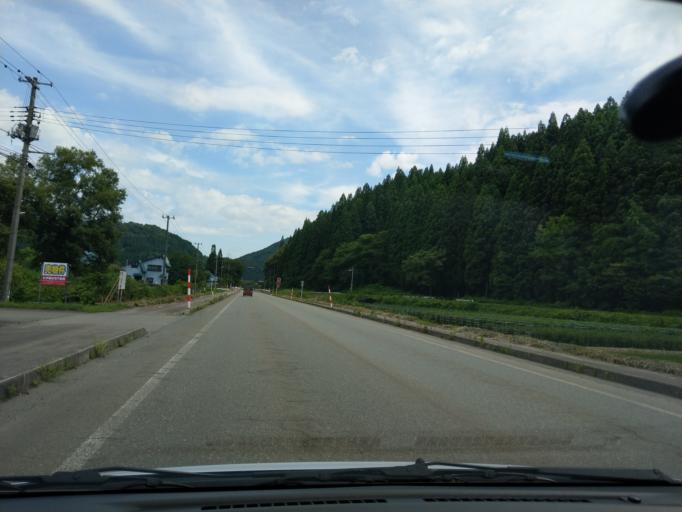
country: JP
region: Akita
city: Kakunodatemachi
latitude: 39.6861
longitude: 140.5552
